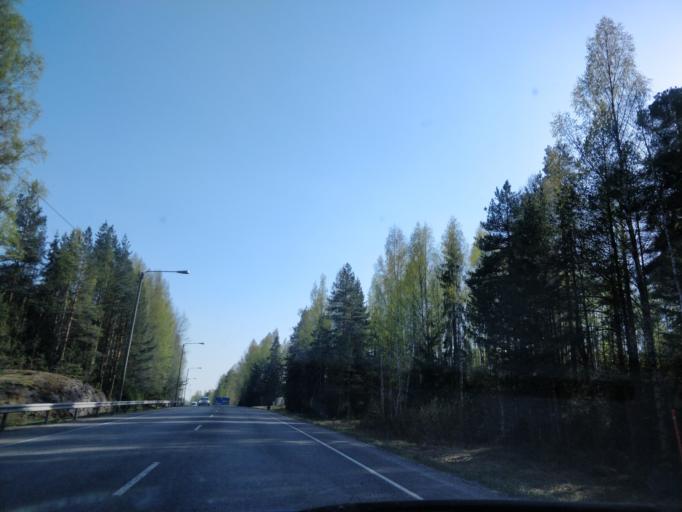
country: FI
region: Uusimaa
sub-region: Helsinki
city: Vantaa
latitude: 60.3092
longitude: 25.1059
